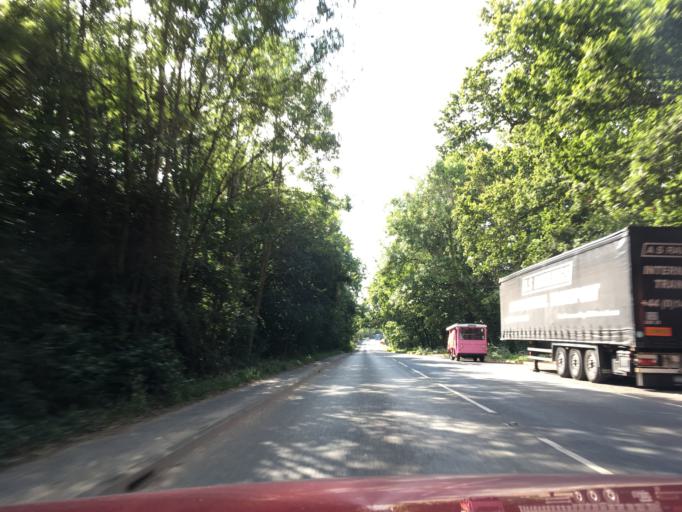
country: GB
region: England
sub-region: Hampshire
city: Bishops Waltham
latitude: 50.9498
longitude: -1.2073
